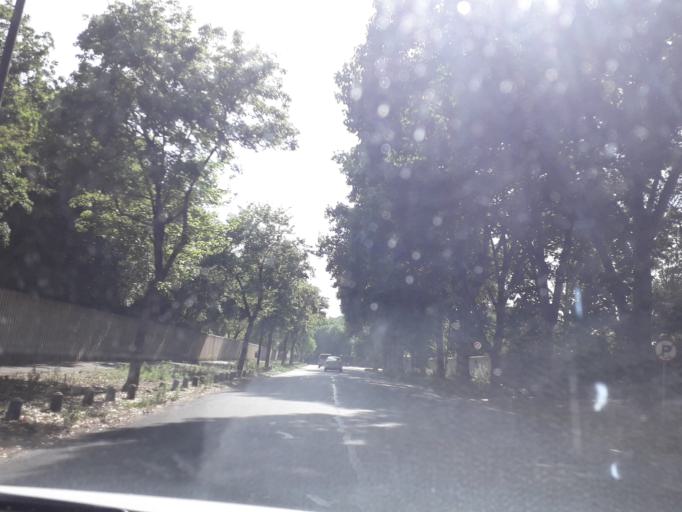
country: ZA
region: Gauteng
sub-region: City of Johannesburg Metropolitan Municipality
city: Johannesburg
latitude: -26.1693
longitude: 28.0388
